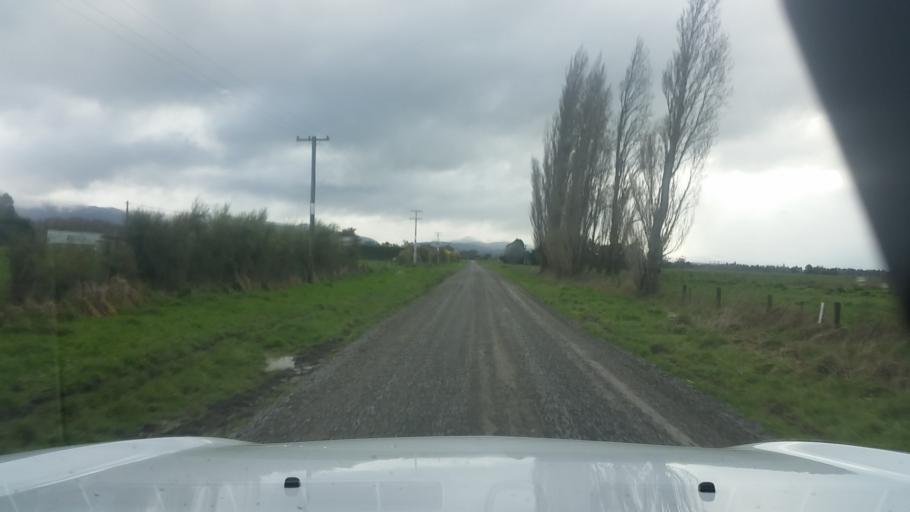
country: NZ
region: Wellington
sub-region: South Wairarapa District
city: Waipawa
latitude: -41.1568
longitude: 175.4199
